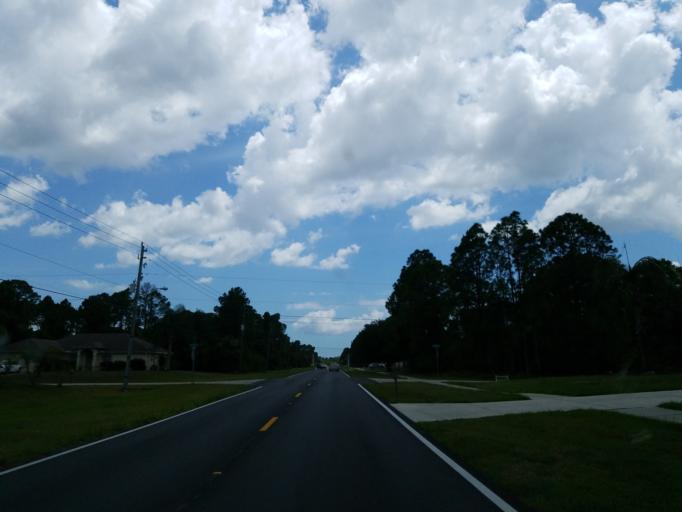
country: US
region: Florida
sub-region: Sarasota County
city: North Port
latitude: 27.0726
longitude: -82.1841
